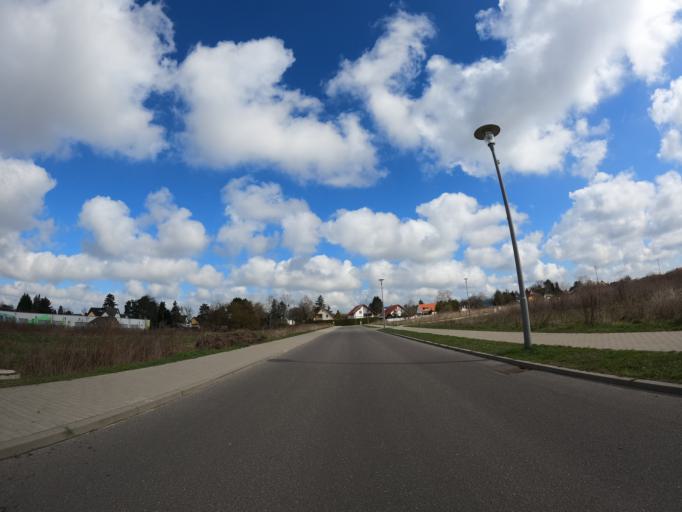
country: DE
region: Brandenburg
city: Hoppegarten
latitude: 52.5195
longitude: 13.6396
